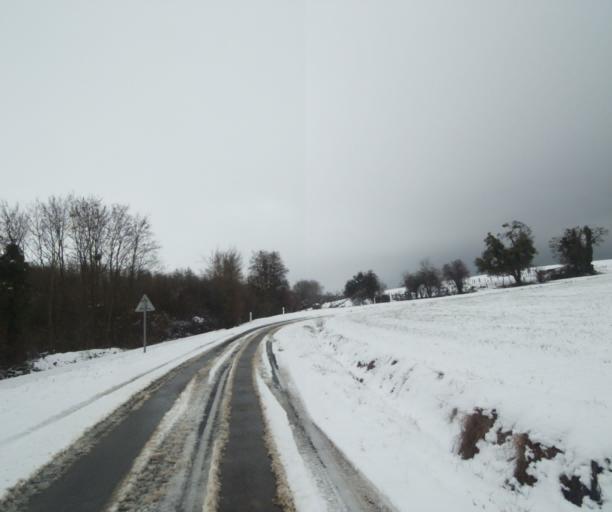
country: FR
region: Champagne-Ardenne
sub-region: Departement de la Haute-Marne
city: Wassy
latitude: 48.4711
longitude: 4.9647
